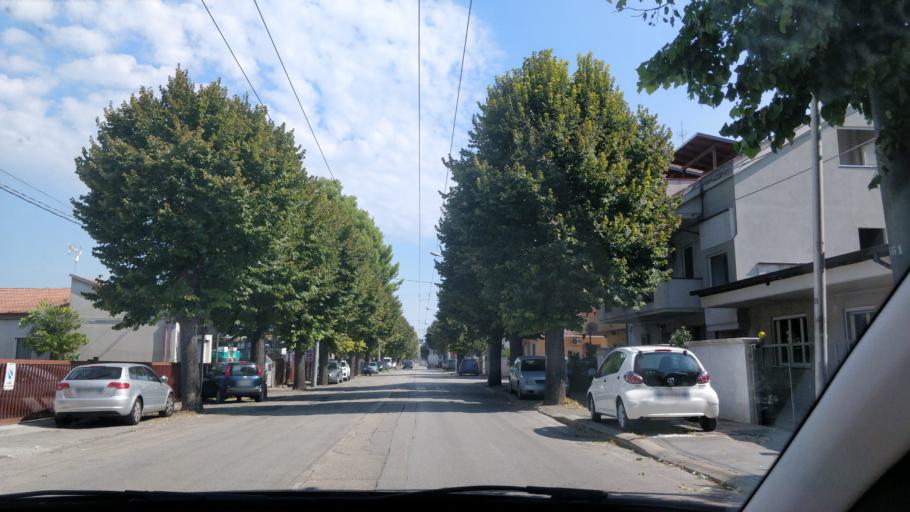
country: IT
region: Abruzzo
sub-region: Provincia di Chieti
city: Chieti
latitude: 42.3777
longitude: 14.1470
